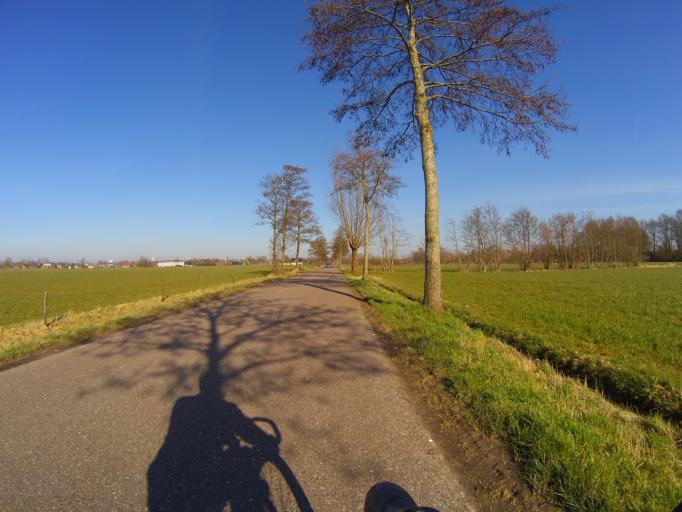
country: NL
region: Gelderland
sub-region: Gemeente Nijkerk
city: Nijkerk
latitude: 52.2082
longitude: 5.4743
